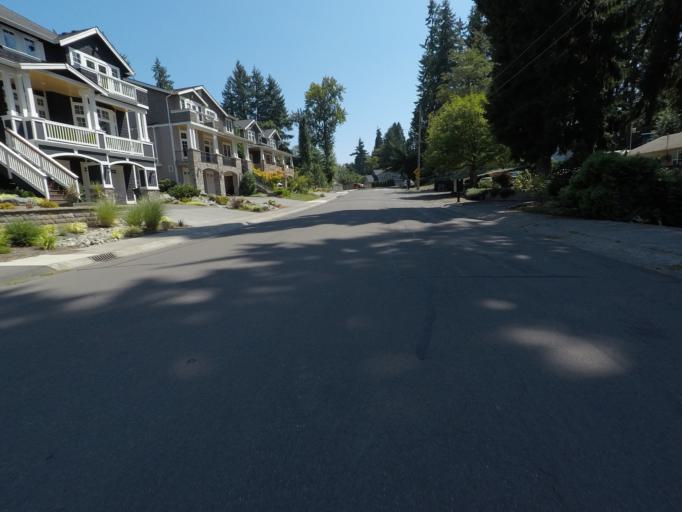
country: US
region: Washington
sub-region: King County
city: Kenmore
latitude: 47.7374
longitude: -122.2437
